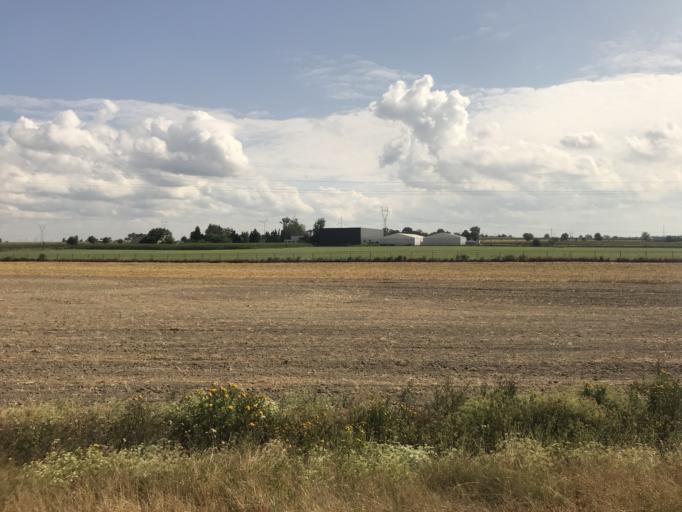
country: PL
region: Kujawsko-Pomorskie
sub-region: Powiat inowroclawski
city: Zlotniki Kujawskie
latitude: 52.9149
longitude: 18.1350
